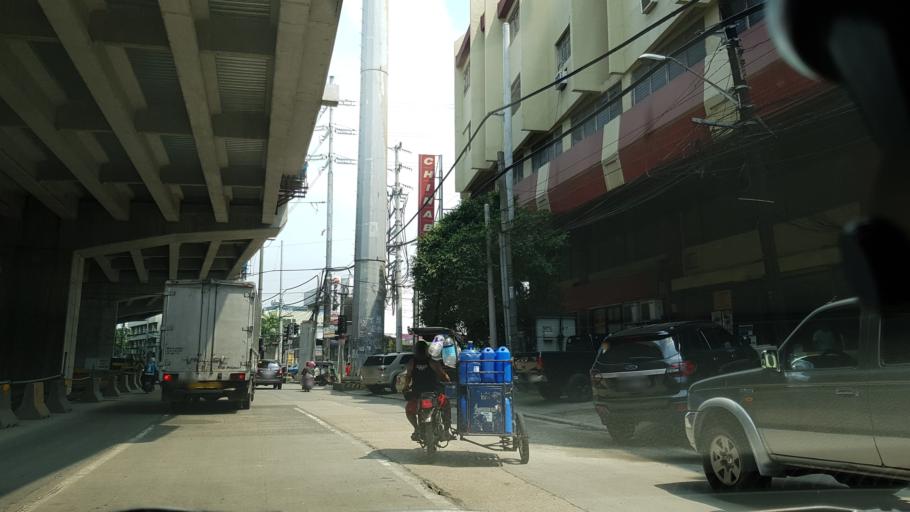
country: PH
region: Metro Manila
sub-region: San Juan
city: San Juan
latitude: 14.6147
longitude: 121.0169
